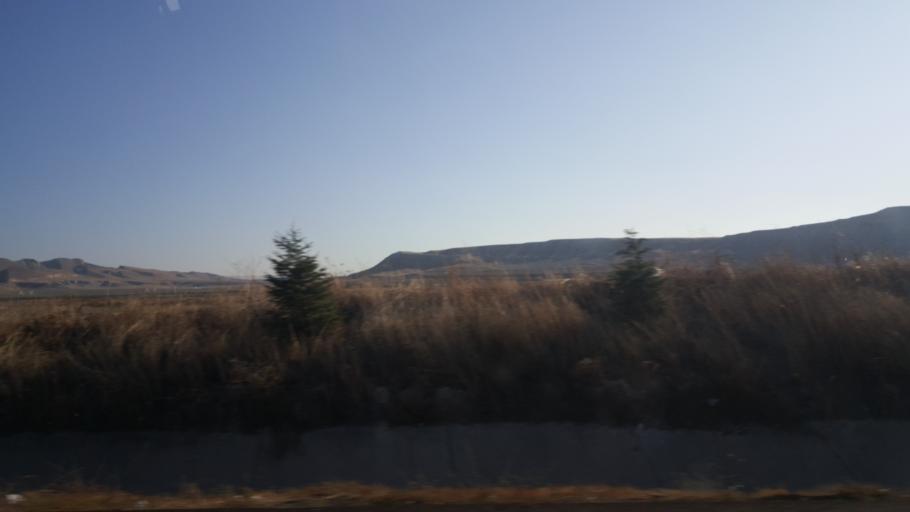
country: TR
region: Ankara
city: Polatli
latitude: 39.5747
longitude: 32.0148
